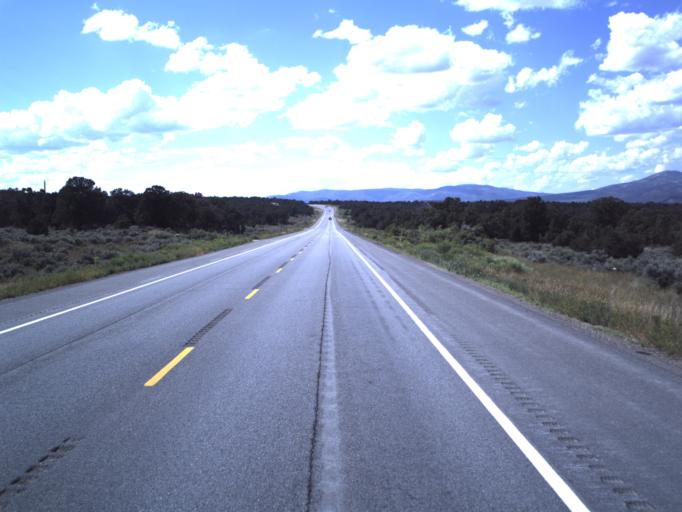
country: US
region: Utah
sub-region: Duchesne County
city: Duchesne
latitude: 40.1921
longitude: -110.6815
